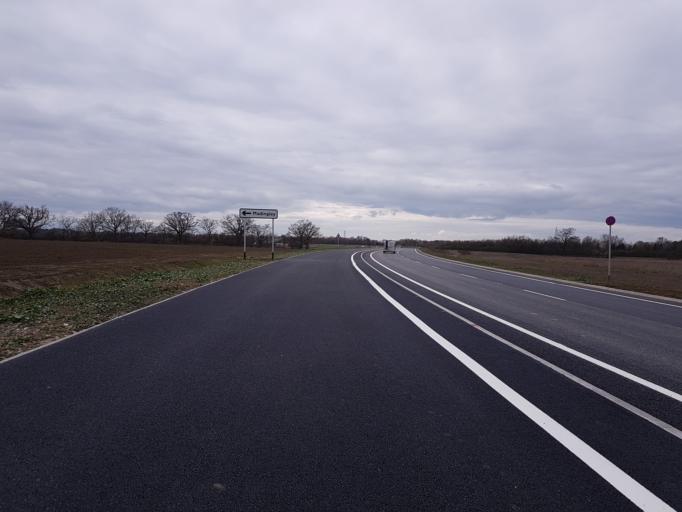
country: GB
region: England
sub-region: Cambridgeshire
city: Girton
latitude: 52.2359
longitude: 0.0596
